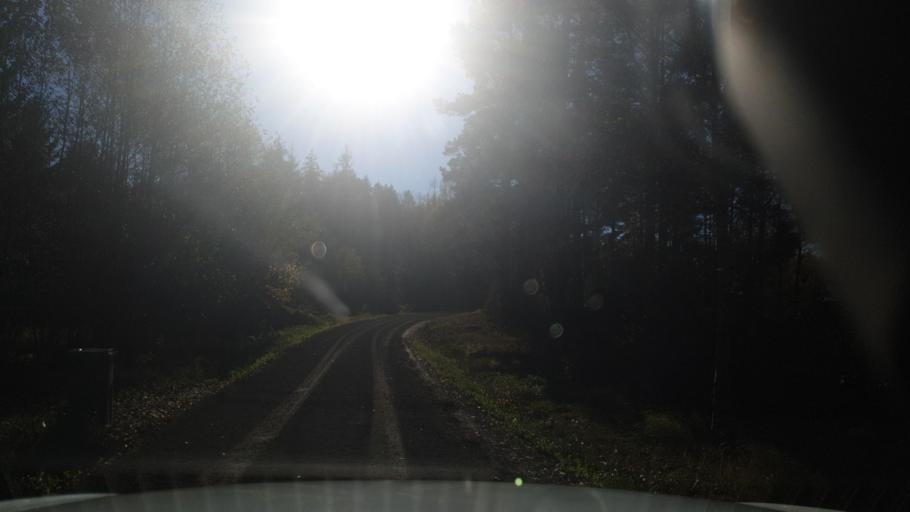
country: SE
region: Vaermland
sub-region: Grums Kommun
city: Grums
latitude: 59.4814
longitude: 12.9300
